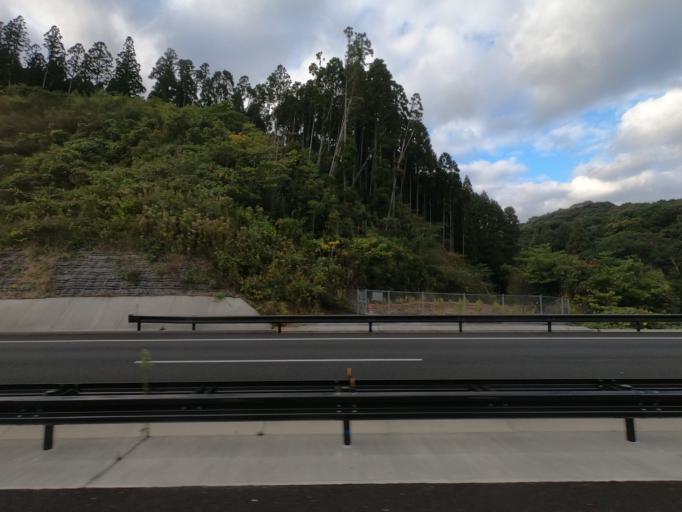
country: JP
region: Kumamoto
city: Minamata
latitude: 32.2398
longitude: 130.4622
